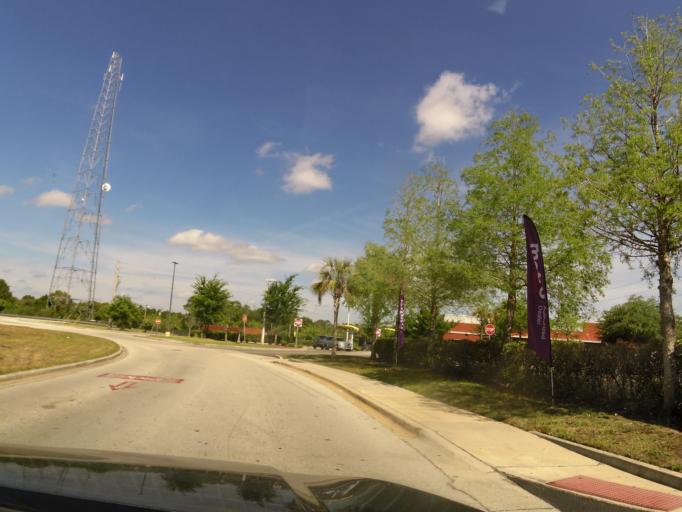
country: US
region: Florida
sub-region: Volusia County
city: Deltona
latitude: 28.8719
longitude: -81.1646
